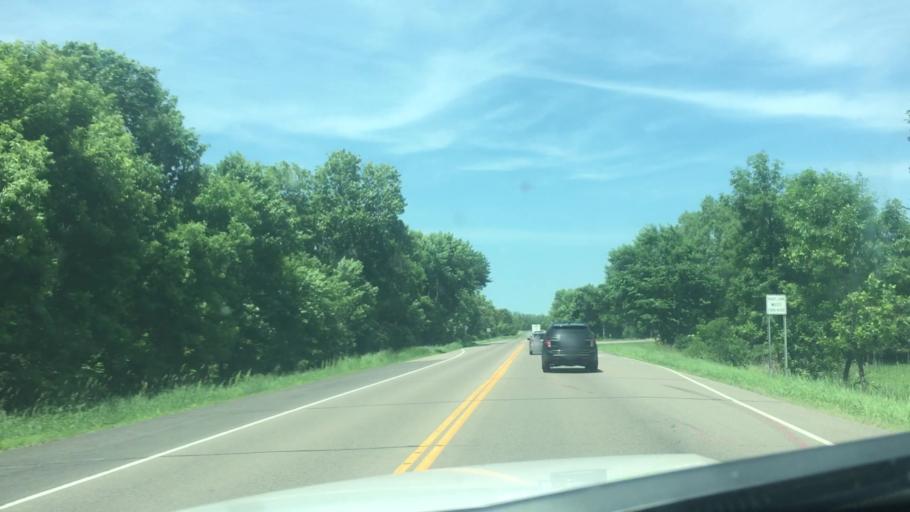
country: US
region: Minnesota
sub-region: Ramsey County
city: White Bear Lake
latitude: 45.1106
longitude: -92.9993
